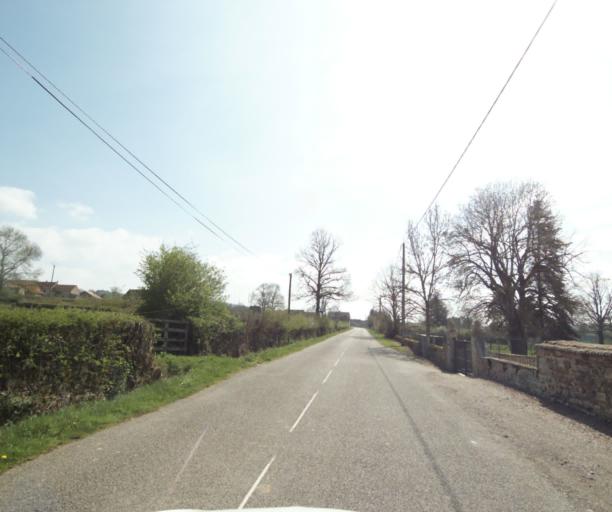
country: FR
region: Bourgogne
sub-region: Departement de Saone-et-Loire
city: Charolles
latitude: 46.3871
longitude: 4.3265
